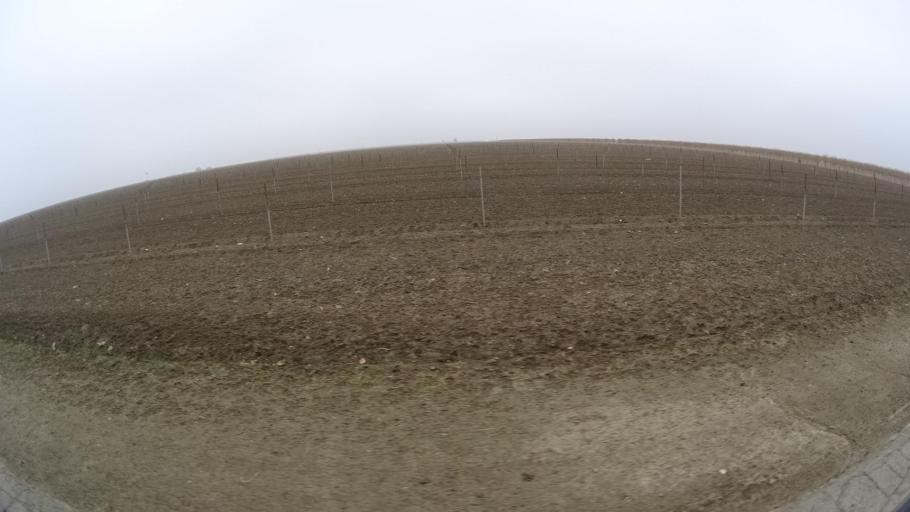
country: US
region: California
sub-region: Tulare County
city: Alpaugh
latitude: 35.6963
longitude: -119.5085
